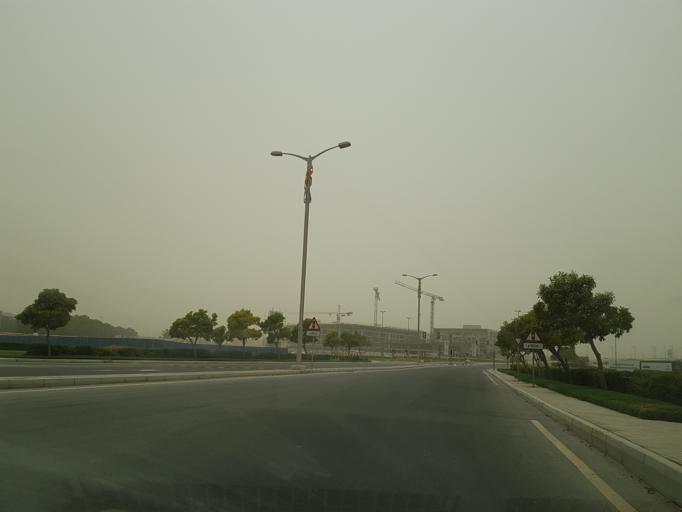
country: AE
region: Dubai
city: Dubai
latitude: 25.1564
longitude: 55.2966
